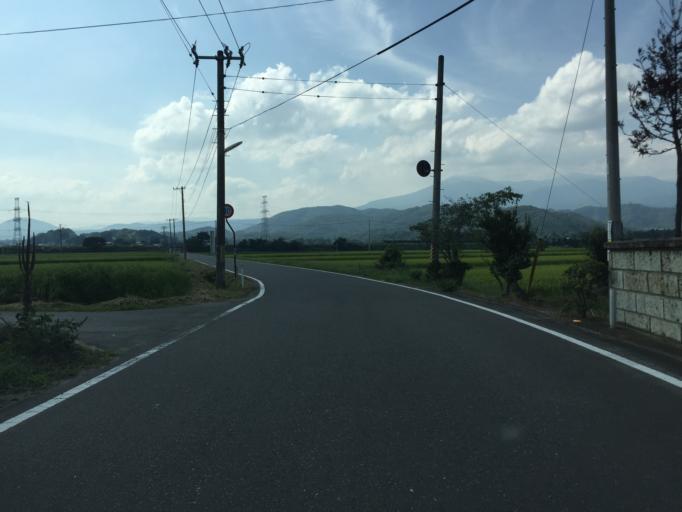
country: JP
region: Fukushima
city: Motomiya
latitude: 37.5565
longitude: 140.3961
